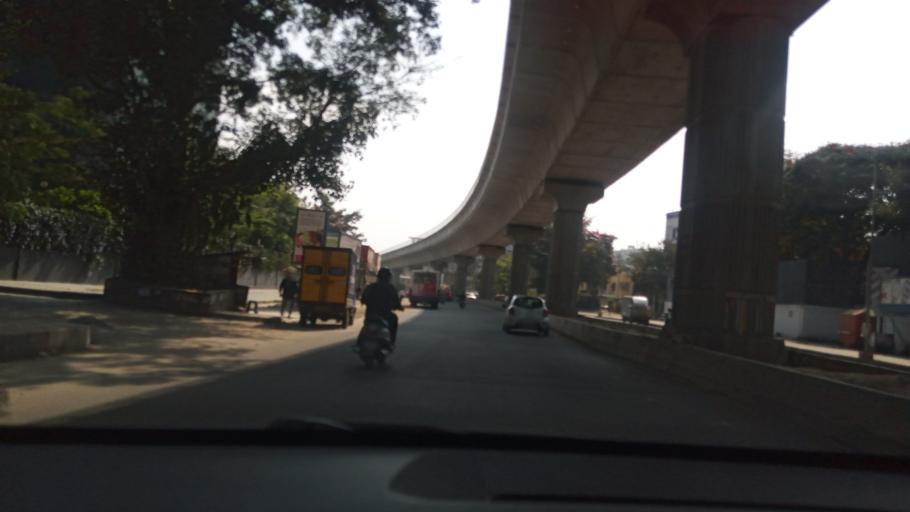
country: IN
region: Karnataka
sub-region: Bangalore Urban
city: Bangalore
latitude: 12.9958
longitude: 77.6947
